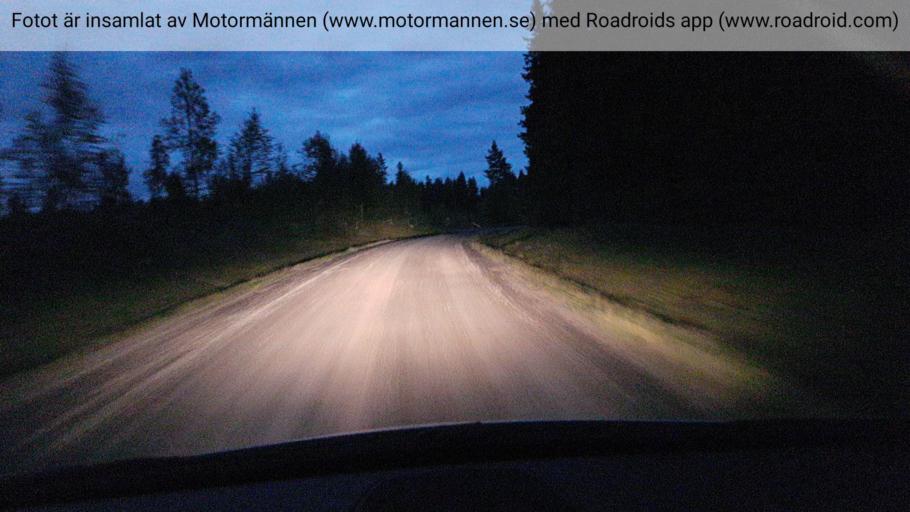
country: SE
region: Jaemtland
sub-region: Braecke Kommun
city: Braecke
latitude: 63.2700
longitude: 15.3771
